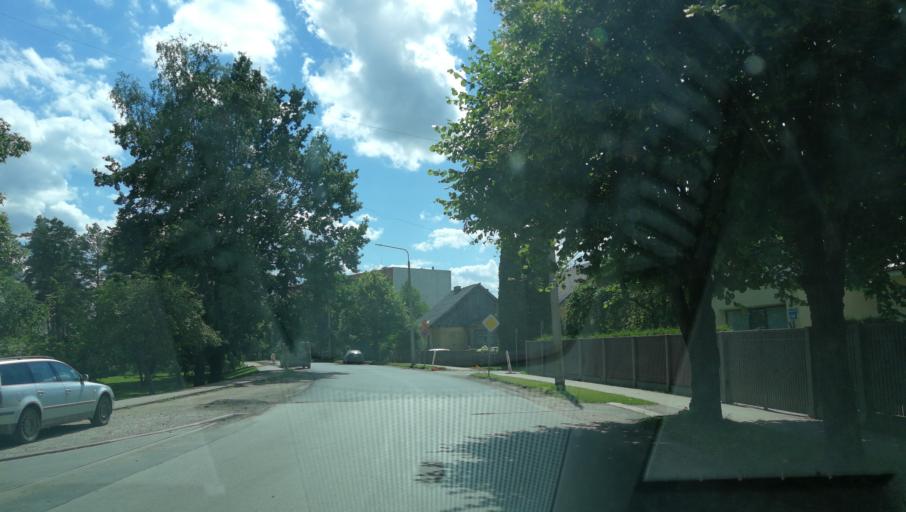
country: LV
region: Broceni
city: Broceni
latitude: 56.6771
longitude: 22.5689
